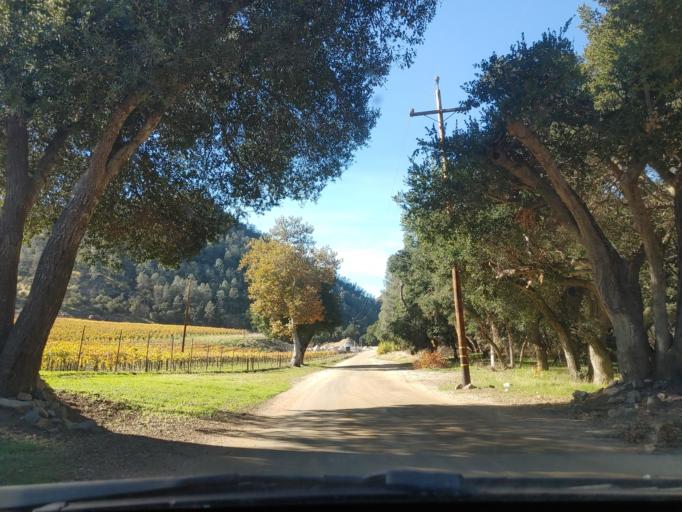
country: US
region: California
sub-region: San Benito County
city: Ridgemark
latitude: 36.6876
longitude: -121.3450
